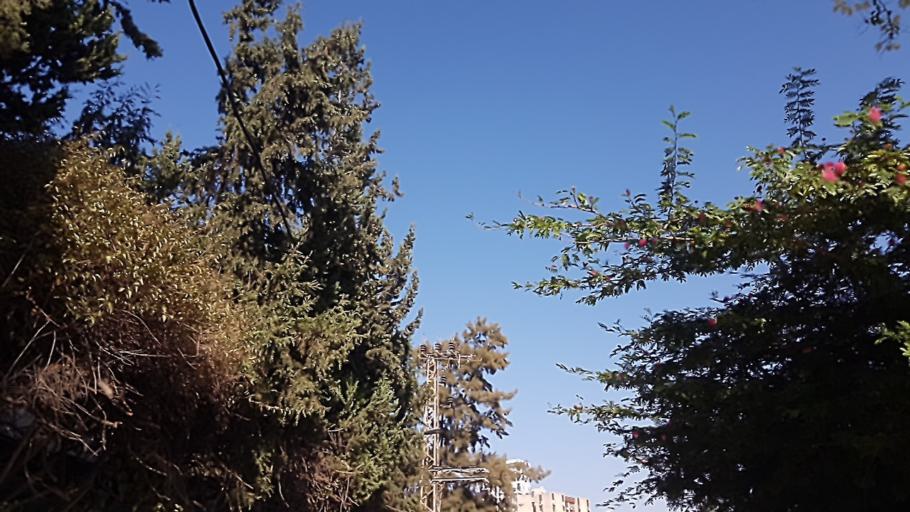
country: IL
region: Tel Aviv
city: Giv`atayim
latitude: 32.0584
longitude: 34.8254
